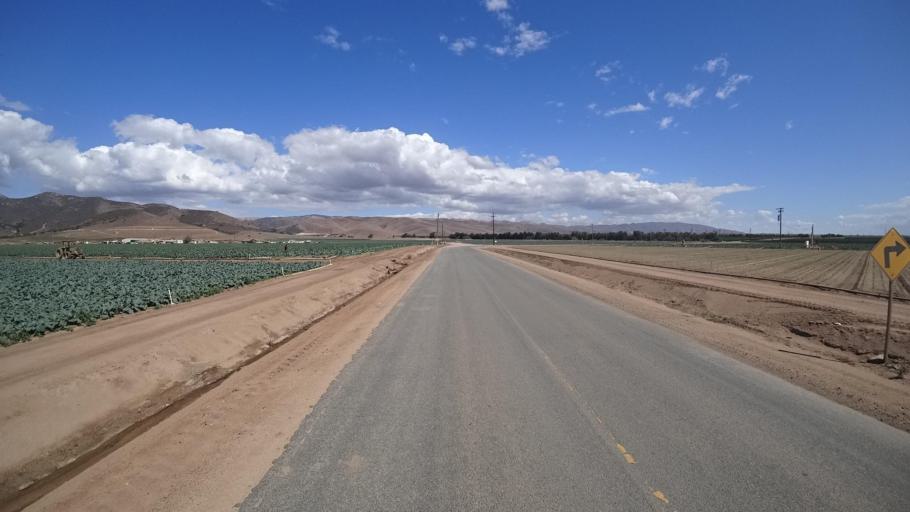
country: US
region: California
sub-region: Monterey County
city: Gonzales
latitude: 36.5579
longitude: -121.4490
